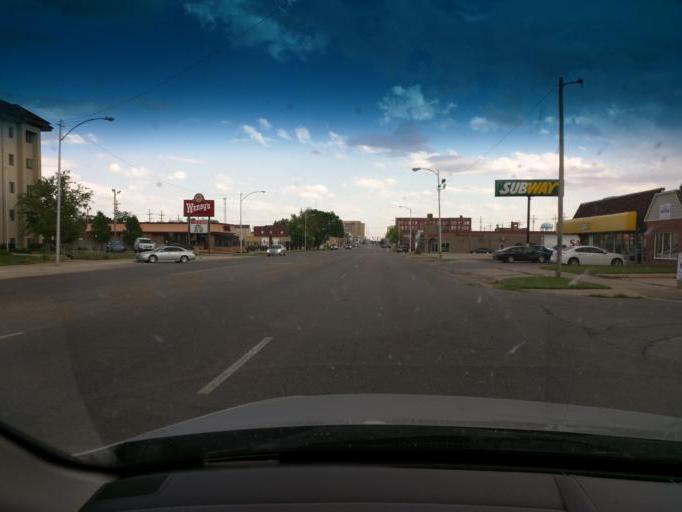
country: US
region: Kansas
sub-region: Reno County
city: Hutchinson
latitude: 38.0619
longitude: -97.9319
